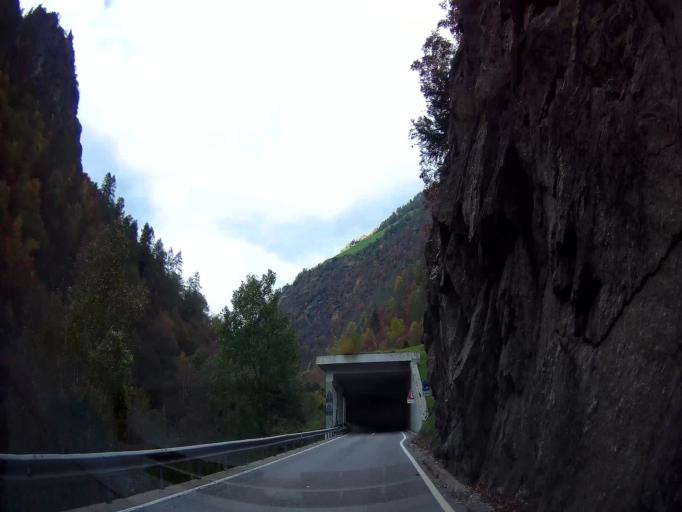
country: IT
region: Trentino-Alto Adige
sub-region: Bolzano
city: Naturno
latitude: 46.6642
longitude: 10.9514
